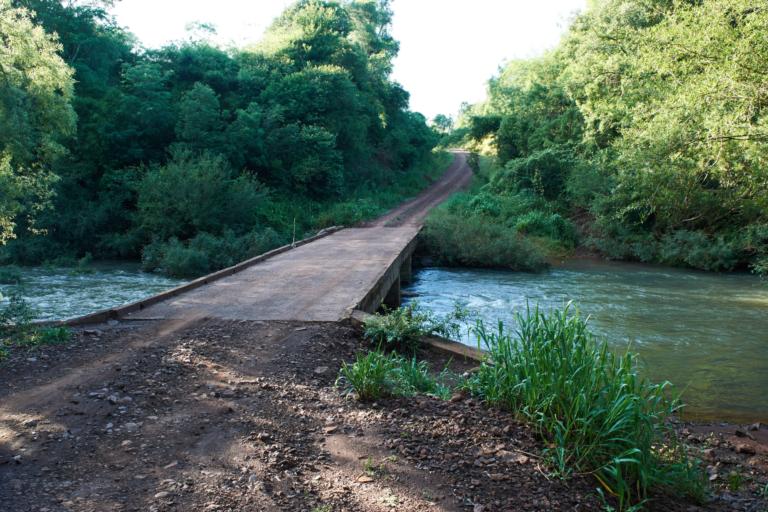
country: AR
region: Misiones
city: Dos de Mayo
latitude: -26.8201
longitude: -54.6298
